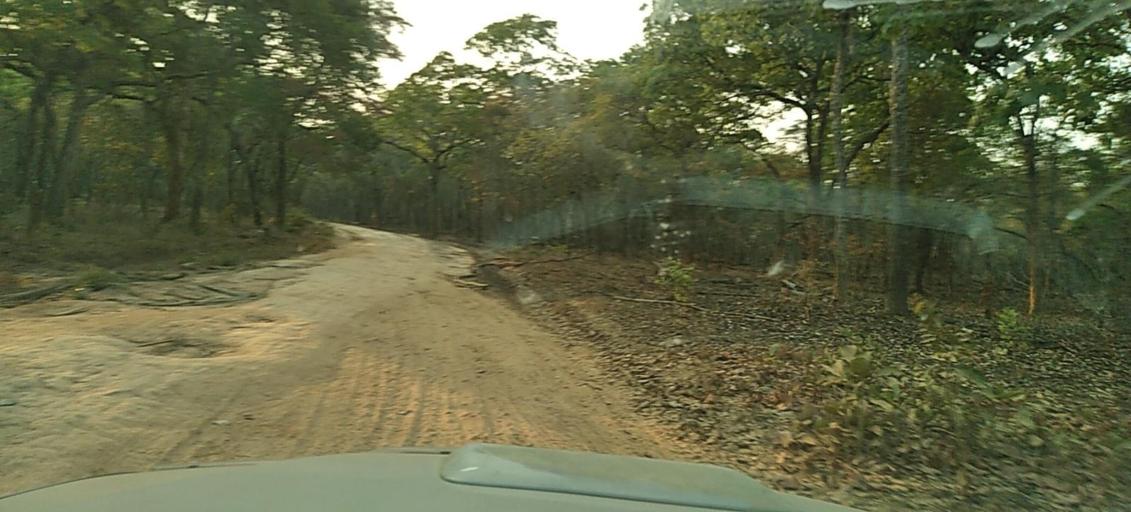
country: ZM
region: North-Western
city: Kasempa
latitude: -13.1580
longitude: 26.4486
